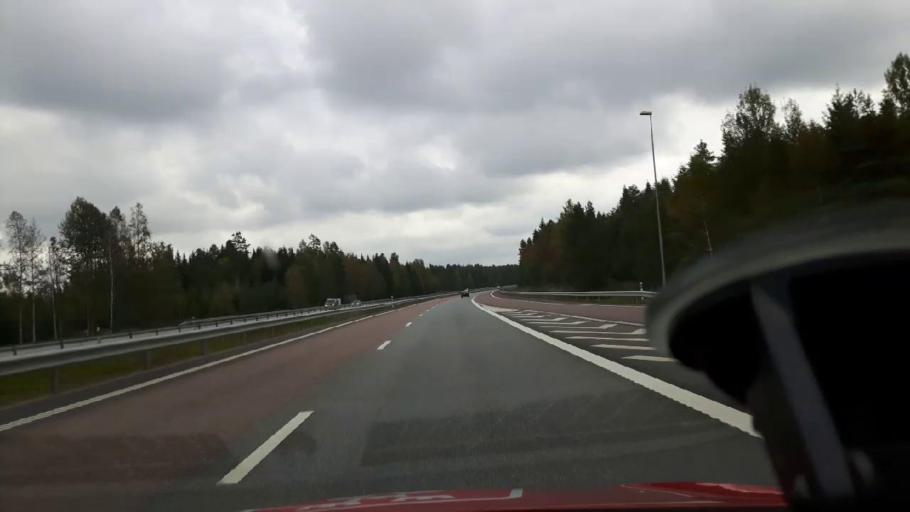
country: SE
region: Gaevleborg
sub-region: Gavle Kommun
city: Gavle
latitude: 60.6376
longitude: 17.1416
